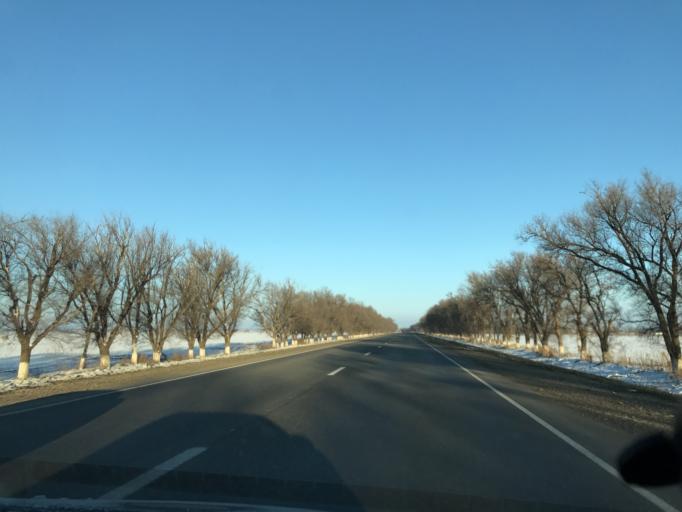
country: RU
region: Stavropol'skiy
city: Bezopasnoye
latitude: 45.6208
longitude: 41.9369
